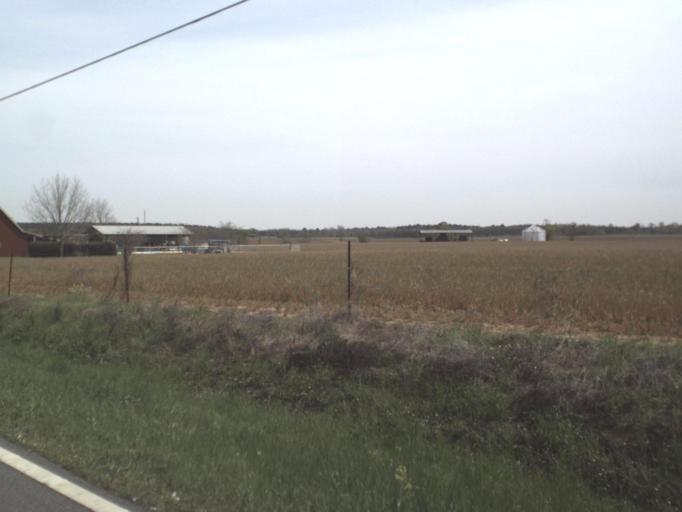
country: US
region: Florida
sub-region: Jackson County
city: Graceville
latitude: 30.9531
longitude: -85.4320
